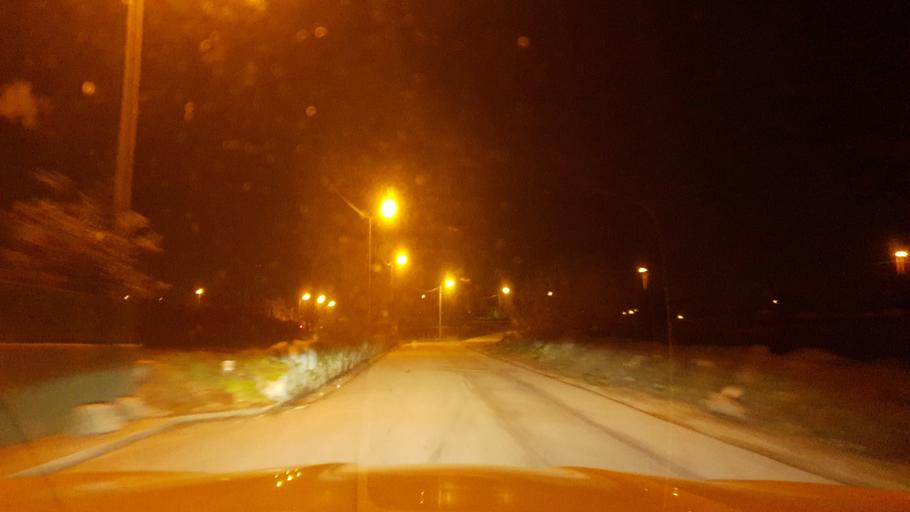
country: PT
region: Porto
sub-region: Matosinhos
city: Senhora da Hora
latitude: 41.2108
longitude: -8.6426
